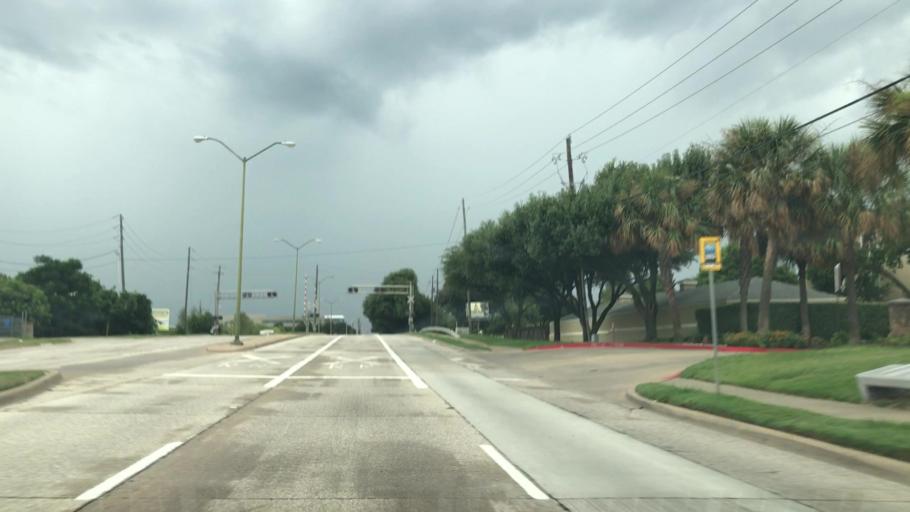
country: US
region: Texas
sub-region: Dallas County
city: Richardson
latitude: 32.9935
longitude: -96.7679
